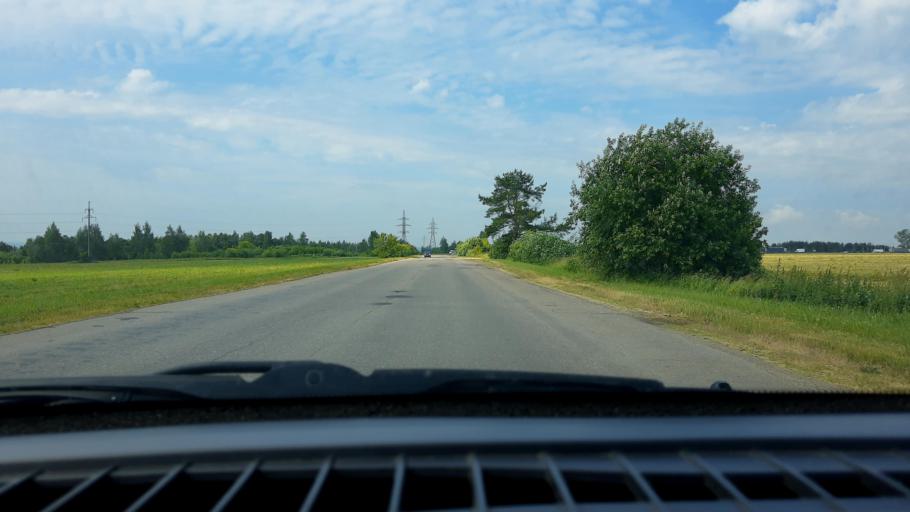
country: RU
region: Nizjnij Novgorod
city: Kstovo
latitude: 56.1111
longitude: 44.2934
